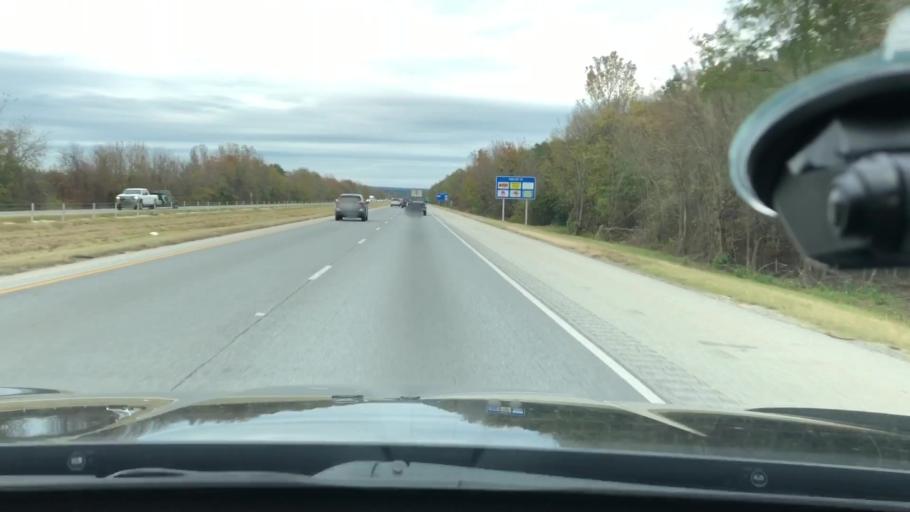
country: US
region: Arkansas
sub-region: Clark County
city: Arkadelphia
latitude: 34.1605
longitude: -93.0768
